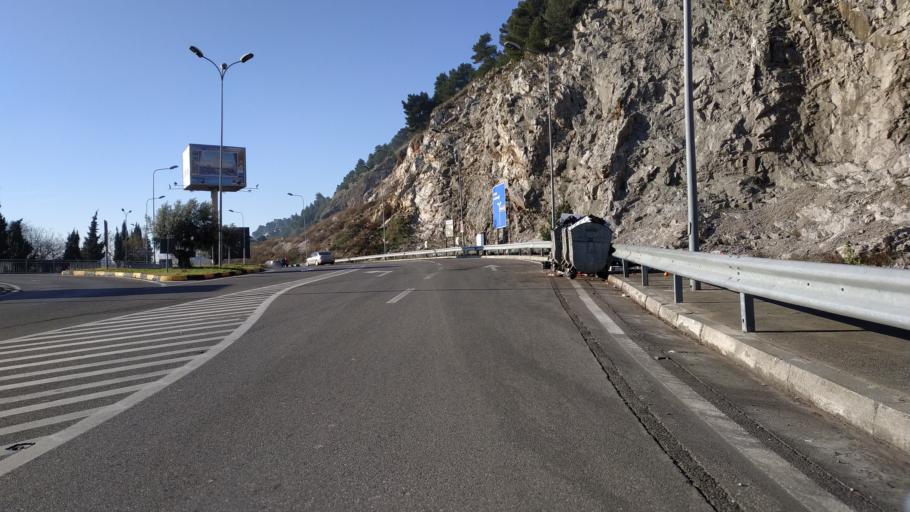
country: AL
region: Shkoder
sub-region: Rrethi i Shkodres
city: Berdica e Madhe
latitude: 42.0466
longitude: 19.4859
